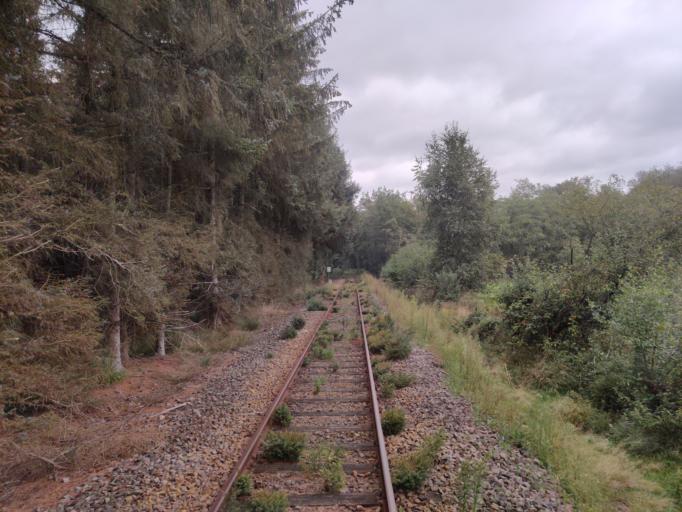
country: DE
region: Lower Saxony
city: Basdahl
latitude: 53.4209
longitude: 9.0169
